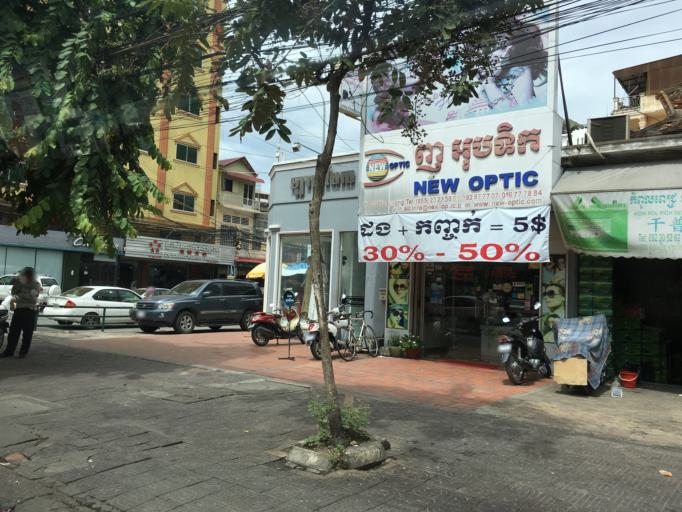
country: KH
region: Phnom Penh
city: Phnom Penh
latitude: 11.5513
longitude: 104.9212
